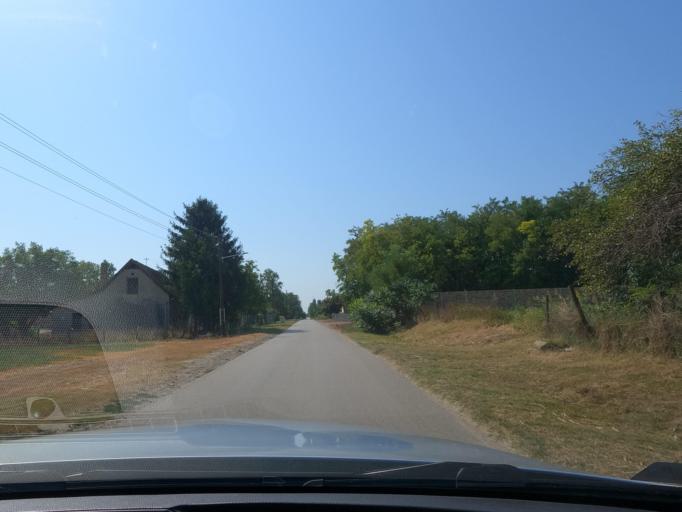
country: HU
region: Csongrad
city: Asotthalom
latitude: 46.0966
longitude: 19.7797
